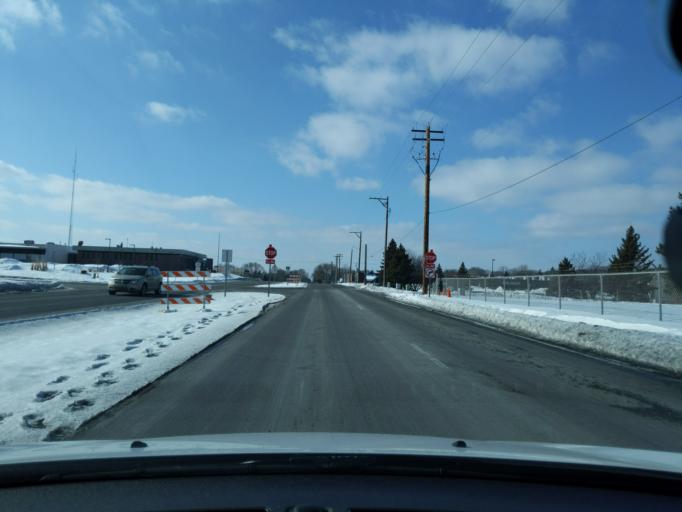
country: US
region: Minnesota
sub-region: Hennepin County
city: Saint Anthony
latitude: 45.0207
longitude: -93.2046
